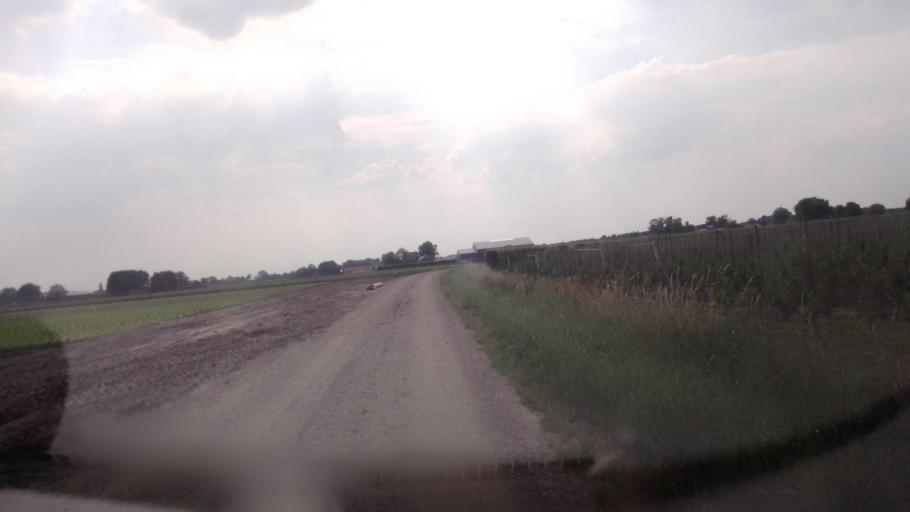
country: NL
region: Limburg
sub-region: Gemeente Peel en Maas
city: Maasbree
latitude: 51.3949
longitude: 6.0334
